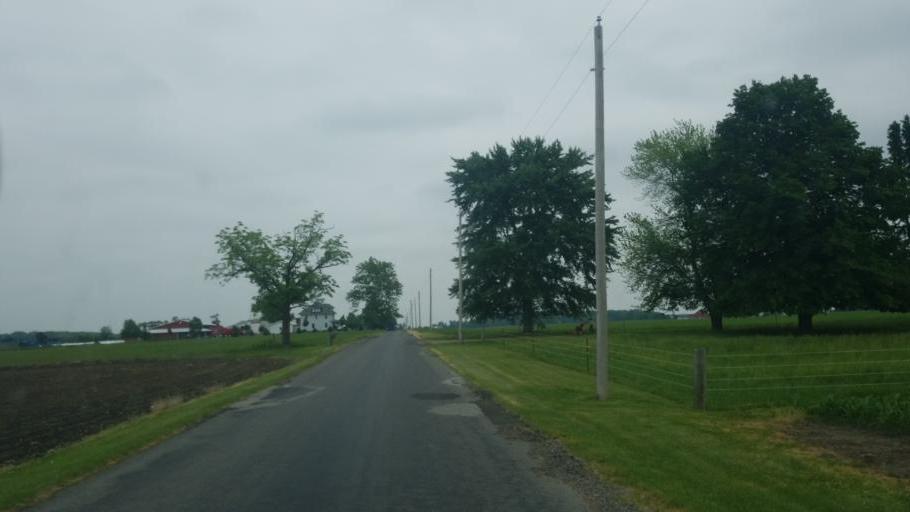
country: US
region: Indiana
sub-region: Elkhart County
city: Wakarusa
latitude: 41.4935
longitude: -86.0700
